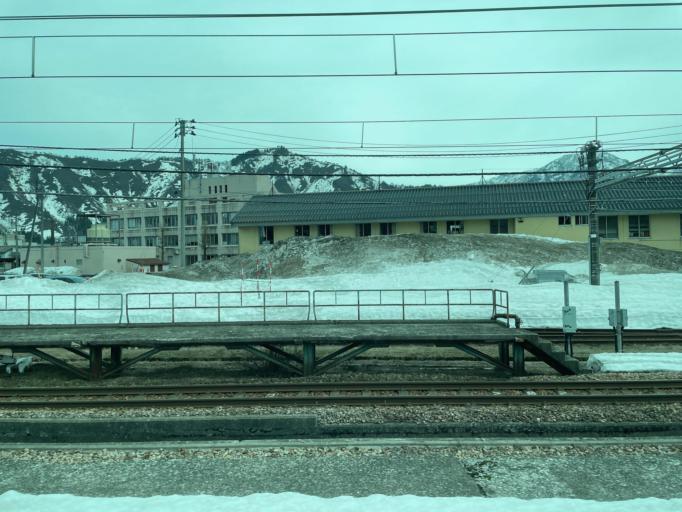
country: JP
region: Niigata
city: Muikamachi
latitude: 37.0658
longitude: 138.8749
